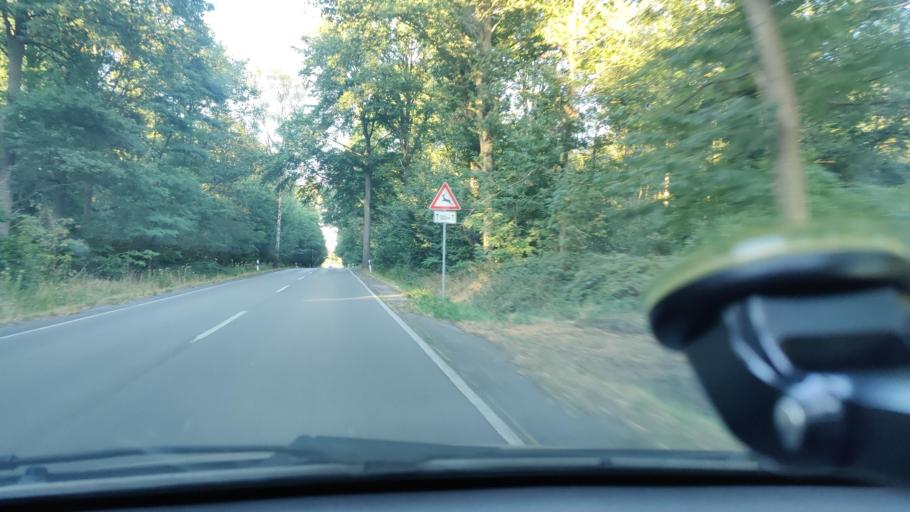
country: DE
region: North Rhine-Westphalia
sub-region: Regierungsbezirk Munster
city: Klein Reken
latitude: 51.7761
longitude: 7.0071
